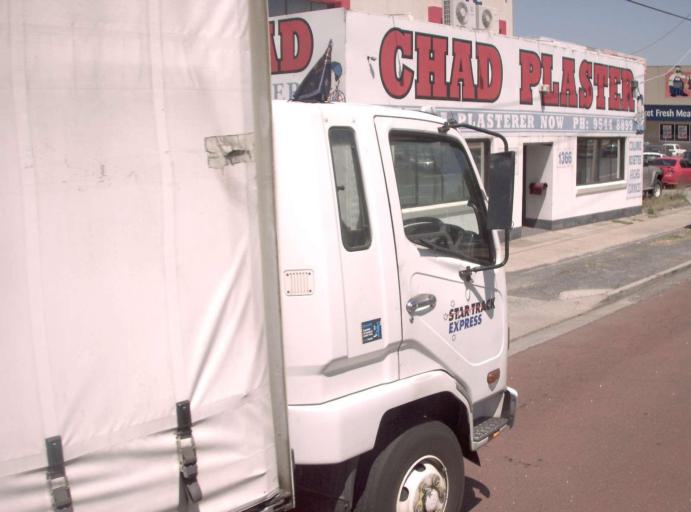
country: AU
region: Victoria
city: Clayton
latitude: -37.9127
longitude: 145.1111
